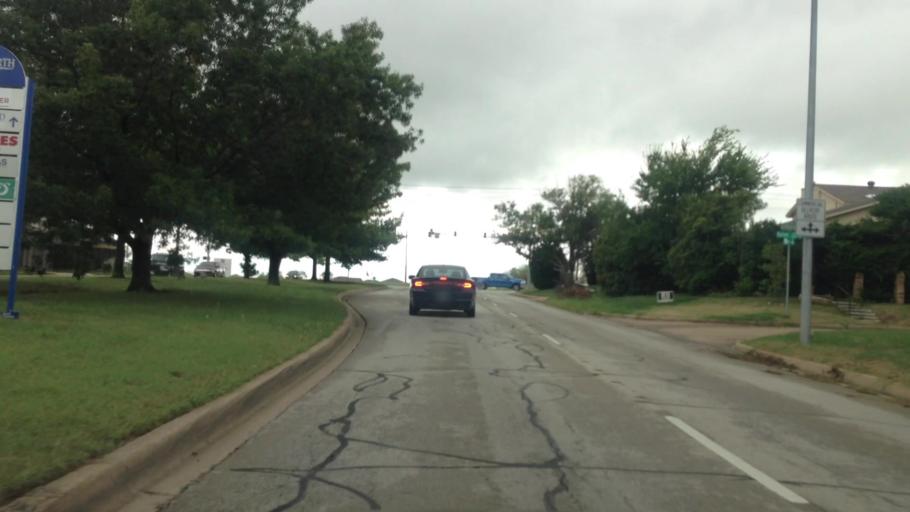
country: US
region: Texas
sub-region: Tarrant County
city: Edgecliff Village
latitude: 32.6291
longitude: -97.3877
